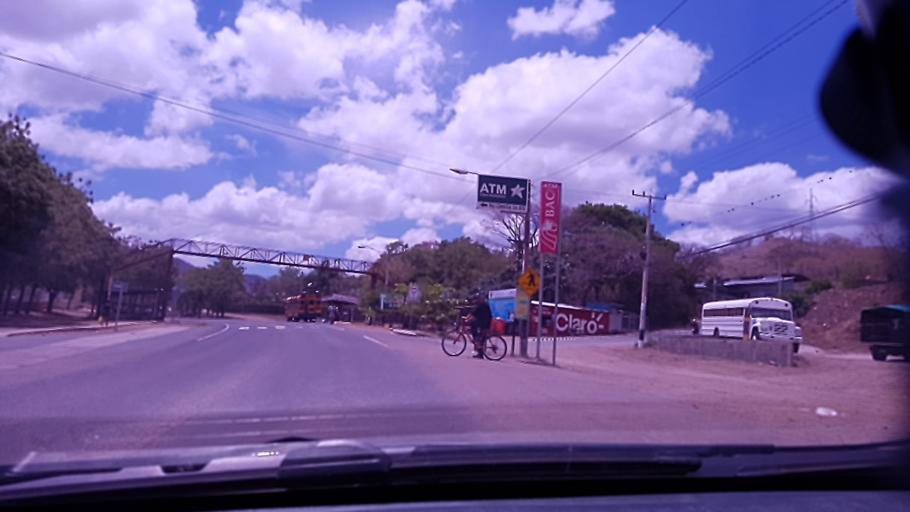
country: NI
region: Esteli
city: Condega
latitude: 13.3613
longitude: -86.4009
